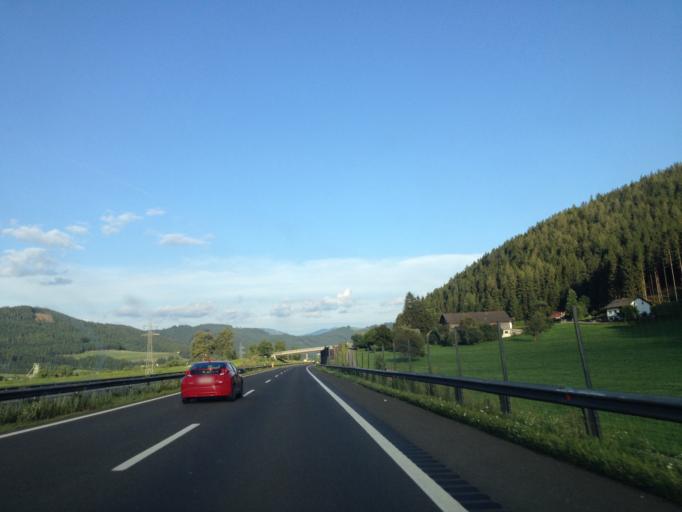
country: AT
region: Styria
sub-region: Politischer Bezirk Leoben
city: Kammern im Liesingtal
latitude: 47.3830
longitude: 14.9333
